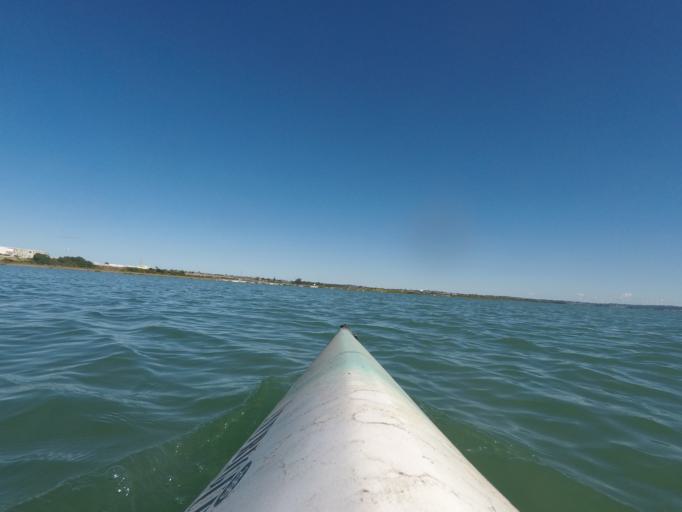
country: NZ
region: Auckland
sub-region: Auckland
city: Rosebank
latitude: -36.8679
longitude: 174.6769
